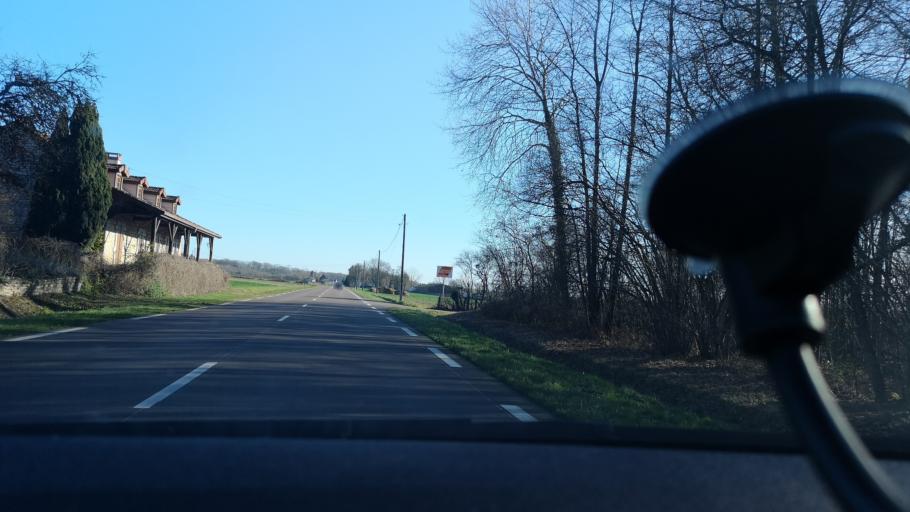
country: FR
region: Bourgogne
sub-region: Departement de Saone-et-Loire
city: Ouroux-sur-Saone
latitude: 46.7740
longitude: 4.9640
